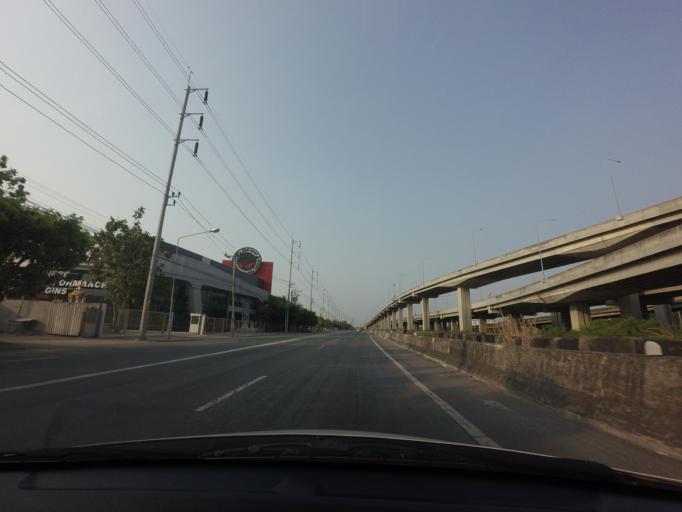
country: TH
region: Samut Prakan
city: Bang Bo District
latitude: 13.6274
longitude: 100.7360
